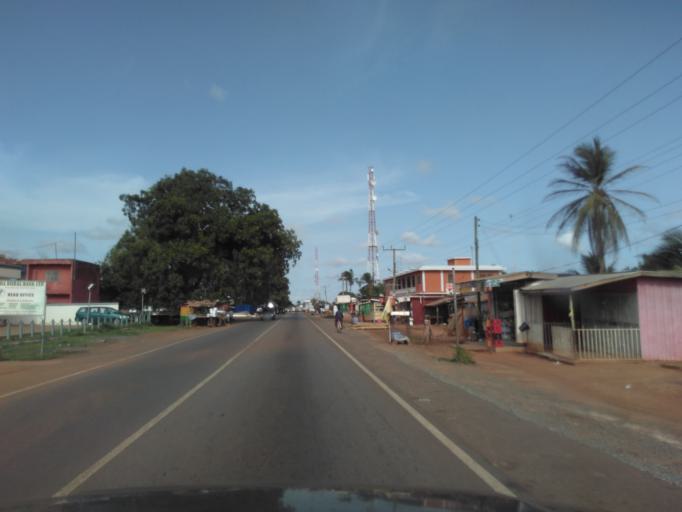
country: GH
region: Volta
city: Anloga
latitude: 5.8961
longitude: 0.5161
